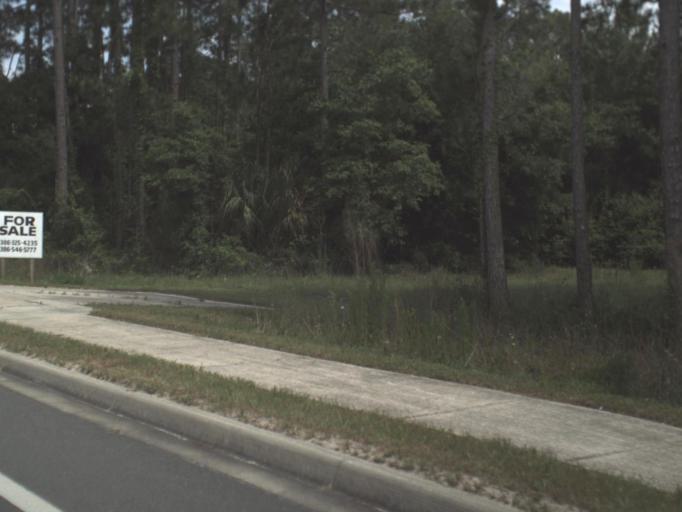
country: US
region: Florida
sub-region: Putnam County
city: Interlachen
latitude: 29.6277
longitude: -81.8464
